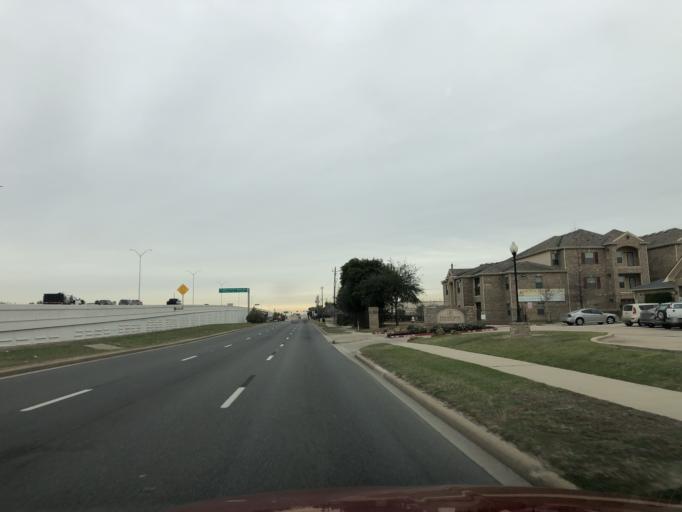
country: US
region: Texas
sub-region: Fort Bend County
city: Missouri City
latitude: 29.6352
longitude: -95.5279
